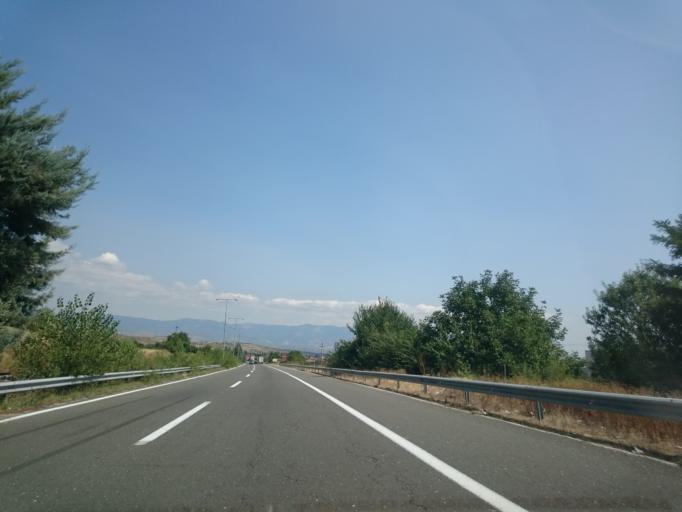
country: MK
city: Ljubin
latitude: 41.9880
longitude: 21.3086
